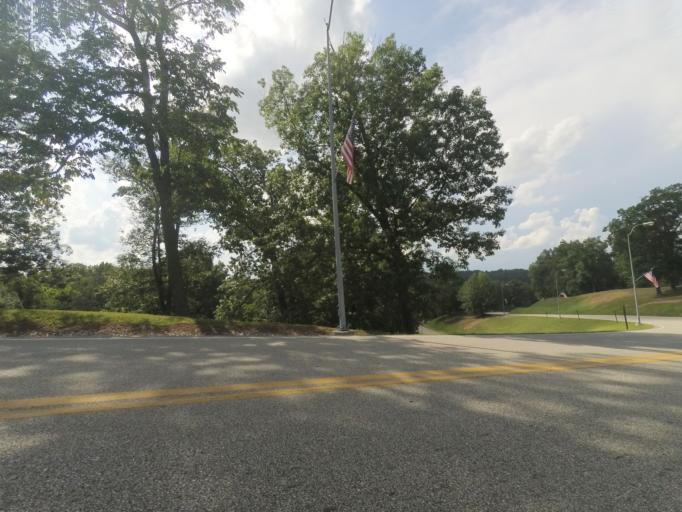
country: US
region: Ohio
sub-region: Lawrence County
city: Burlington
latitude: 38.3789
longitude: -82.5158
